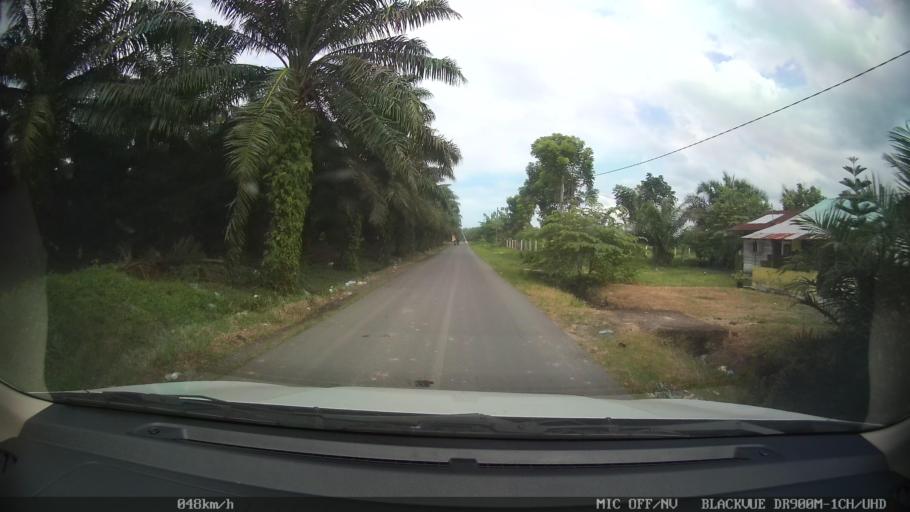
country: ID
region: North Sumatra
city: Sunggal
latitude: 3.6356
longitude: 98.6042
